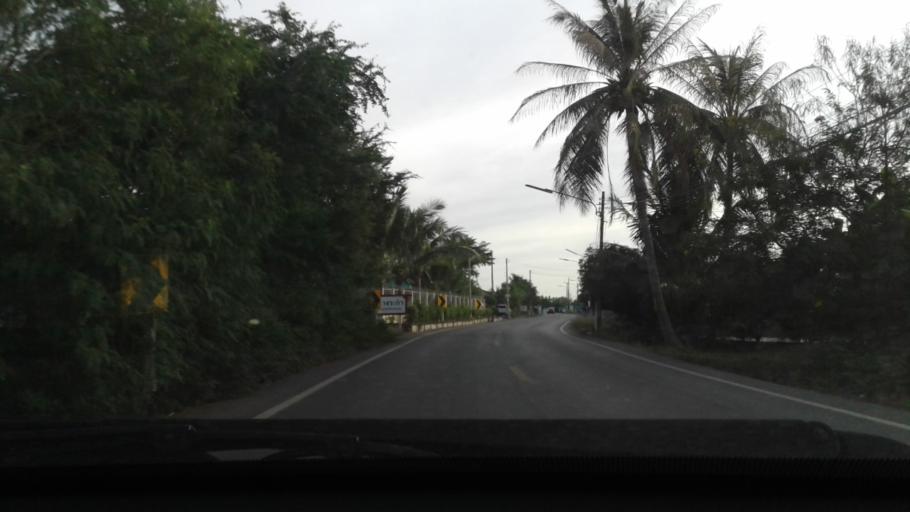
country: TH
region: Nonthaburi
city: Sai Noi
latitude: 13.9064
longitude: 100.2575
